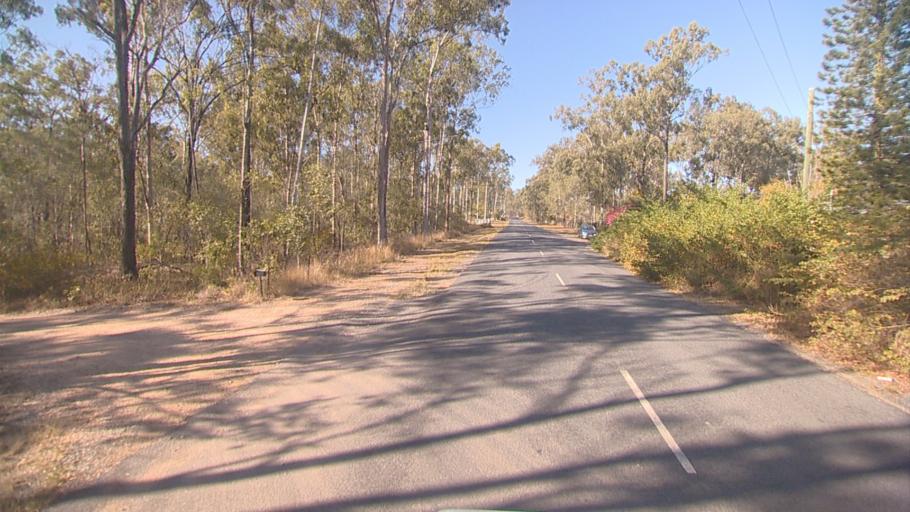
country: AU
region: Queensland
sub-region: Logan
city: Cedar Vale
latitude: -27.8425
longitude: 153.0560
